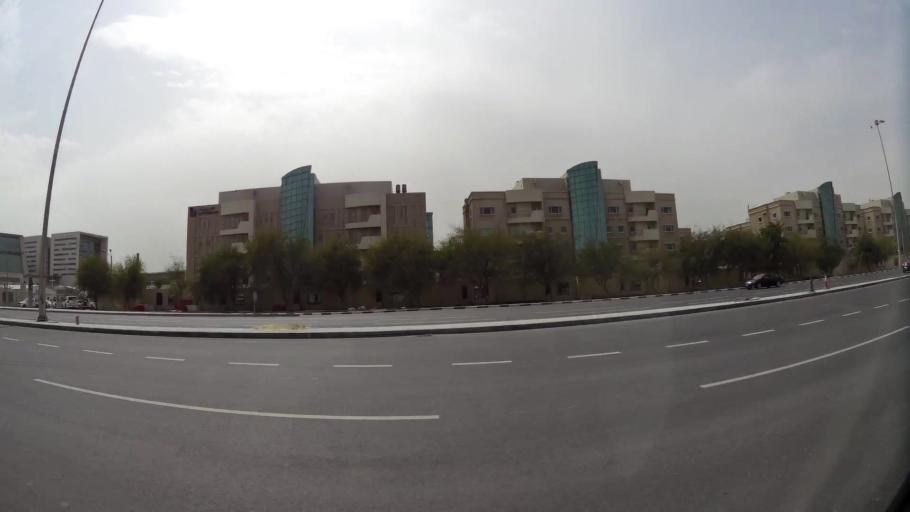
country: QA
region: Baladiyat ad Dawhah
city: Doha
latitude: 25.2993
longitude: 51.5082
